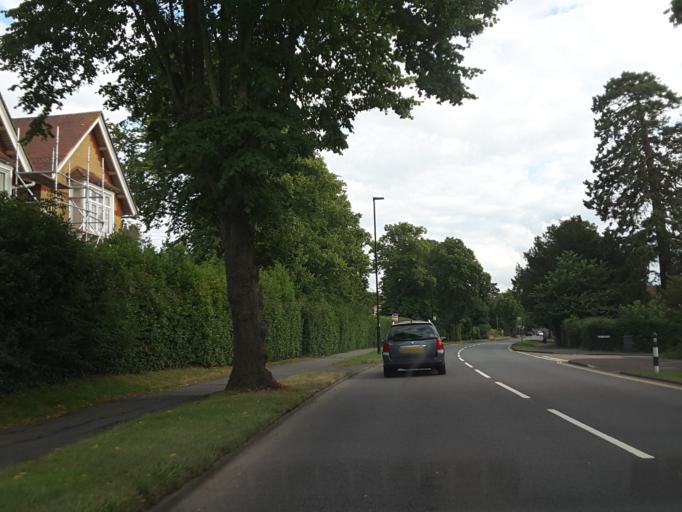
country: GB
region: England
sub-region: Isle of Wight
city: East Cowes
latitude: 50.7528
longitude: -1.2776
